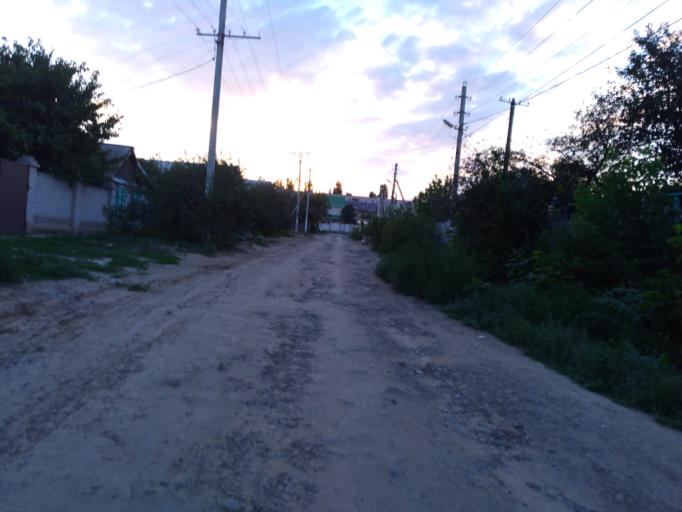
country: RU
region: Volgograd
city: Volgograd
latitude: 48.6699
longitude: 44.4522
